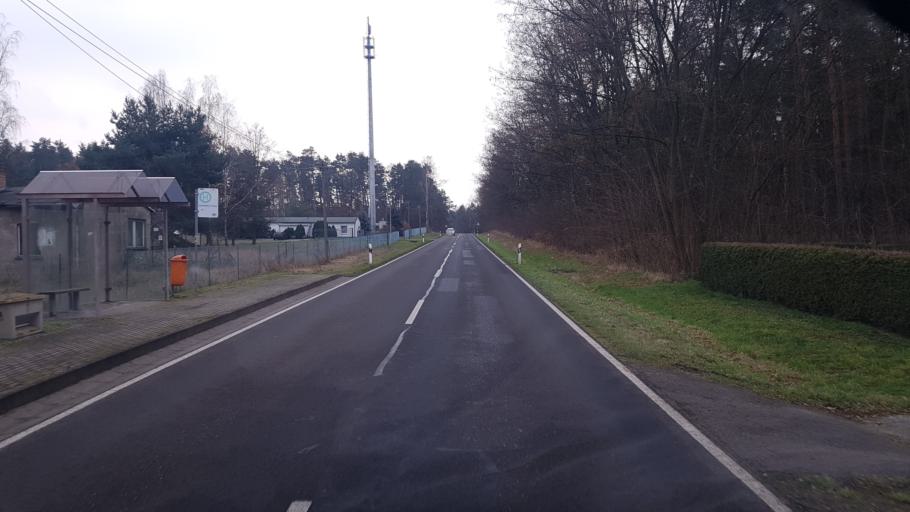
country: DE
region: Brandenburg
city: Schenkendobern
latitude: 51.9503
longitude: 14.6357
